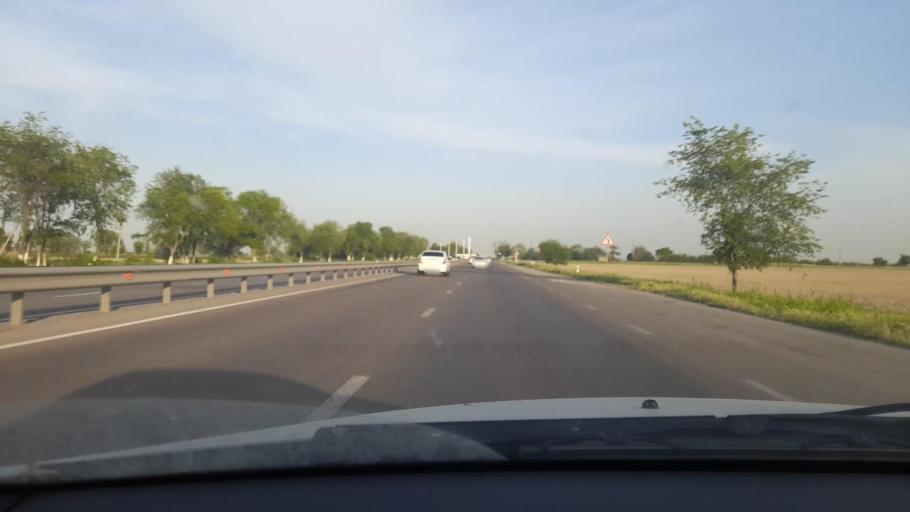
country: KZ
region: Ongtustik Qazaqstan
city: Myrzakent
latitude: 40.5272
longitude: 68.4451
